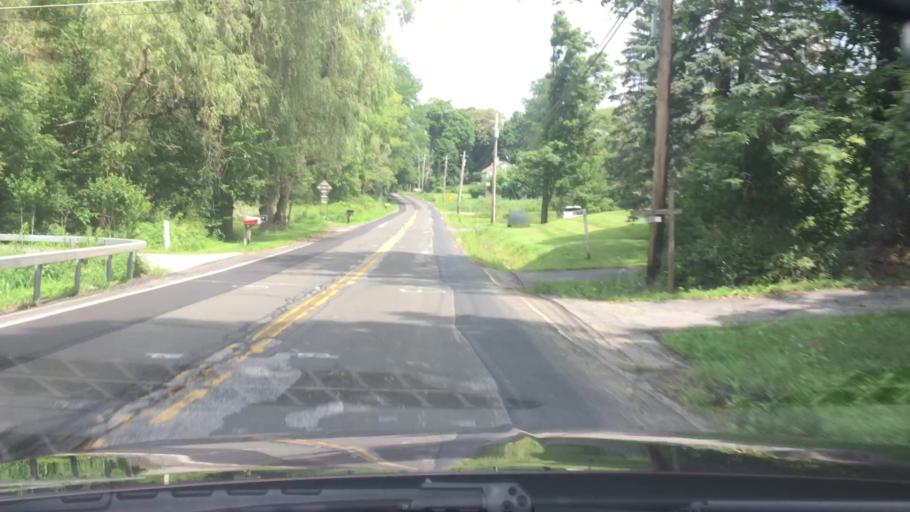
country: US
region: New York
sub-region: Dutchess County
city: Pawling
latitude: 41.5998
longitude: -73.6828
